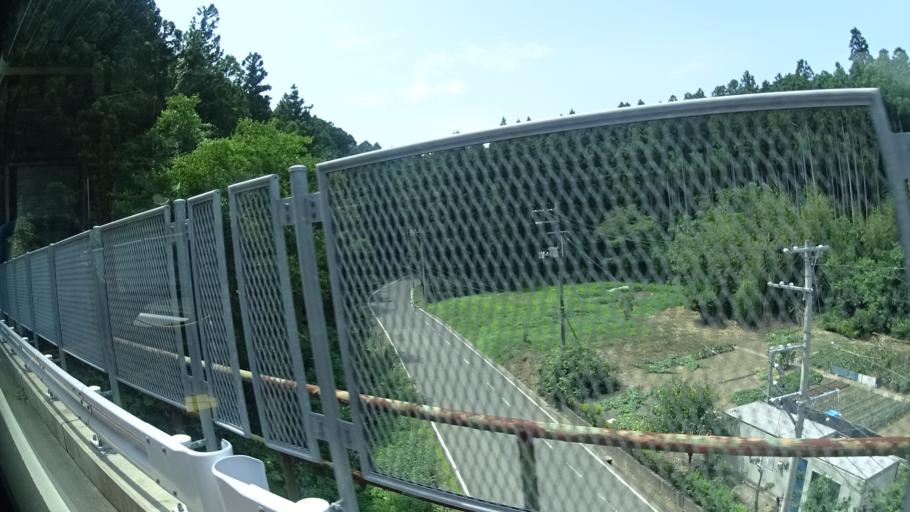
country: JP
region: Miyagi
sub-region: Oshika Gun
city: Onagawa Cho
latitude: 38.6508
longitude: 141.4428
